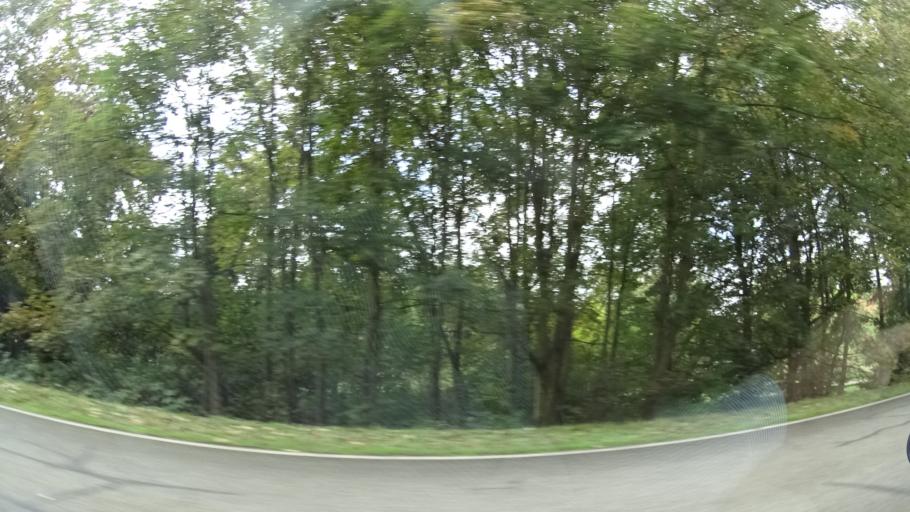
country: DE
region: Baden-Wuerttemberg
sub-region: Karlsruhe Region
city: Ubstadt-Weiher
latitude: 49.1840
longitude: 8.6736
